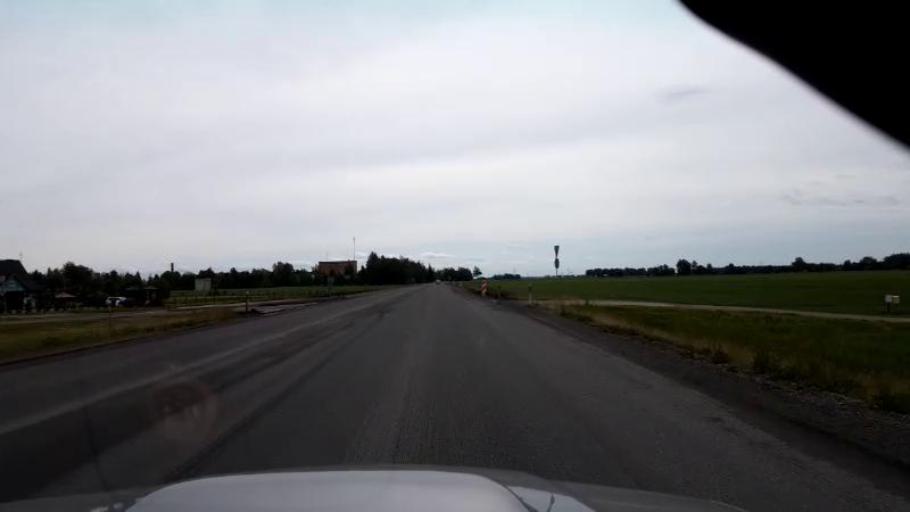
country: LV
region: Bauskas Rajons
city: Bauska
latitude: 56.3121
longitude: 24.3341
